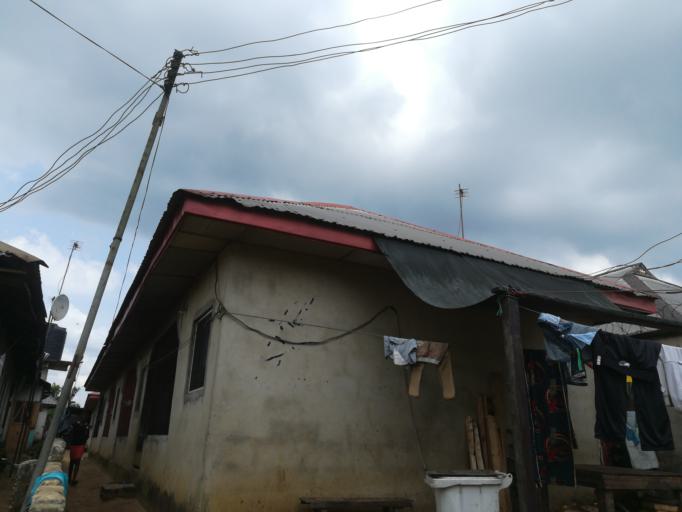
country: NG
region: Rivers
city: Okrika
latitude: 4.7313
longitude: 7.1447
